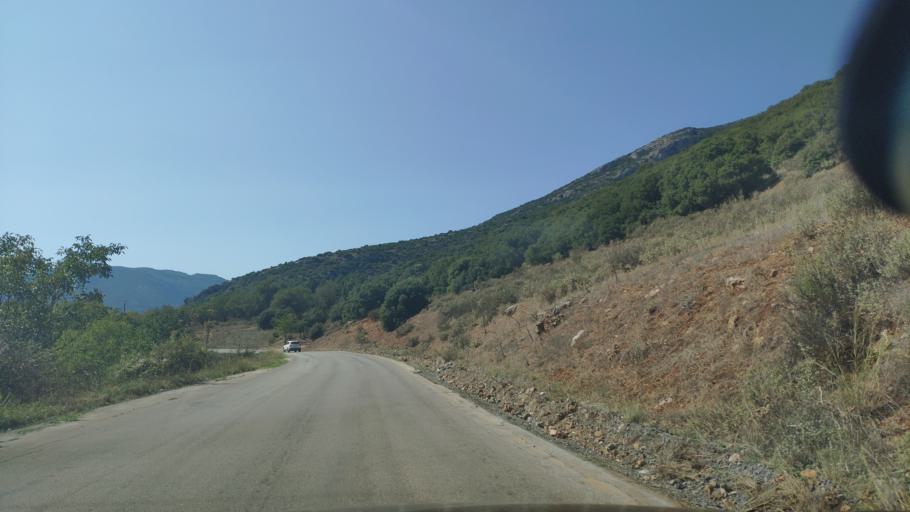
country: GR
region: Peloponnese
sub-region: Nomos Korinthias
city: Nemea
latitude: 37.9092
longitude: 22.5235
